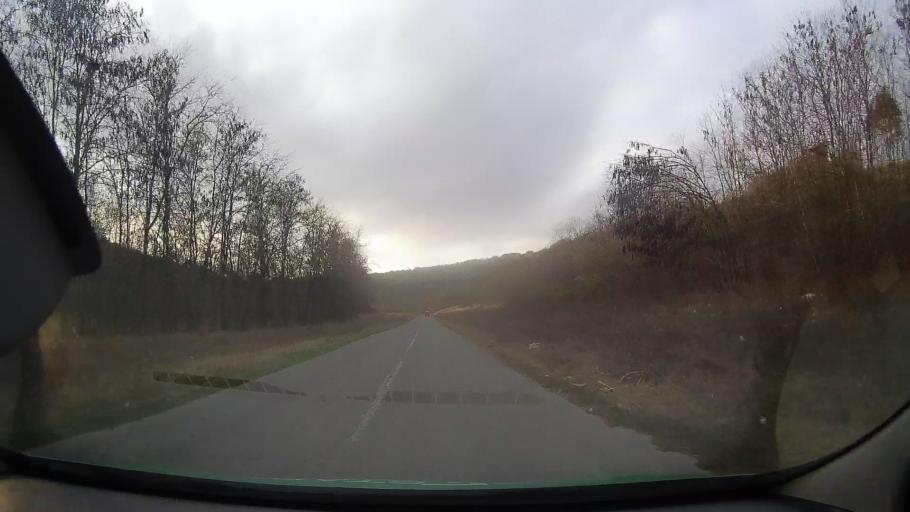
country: RO
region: Constanta
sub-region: Comuna Adamclisi
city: Adamclisi
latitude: 44.0391
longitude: 27.9485
